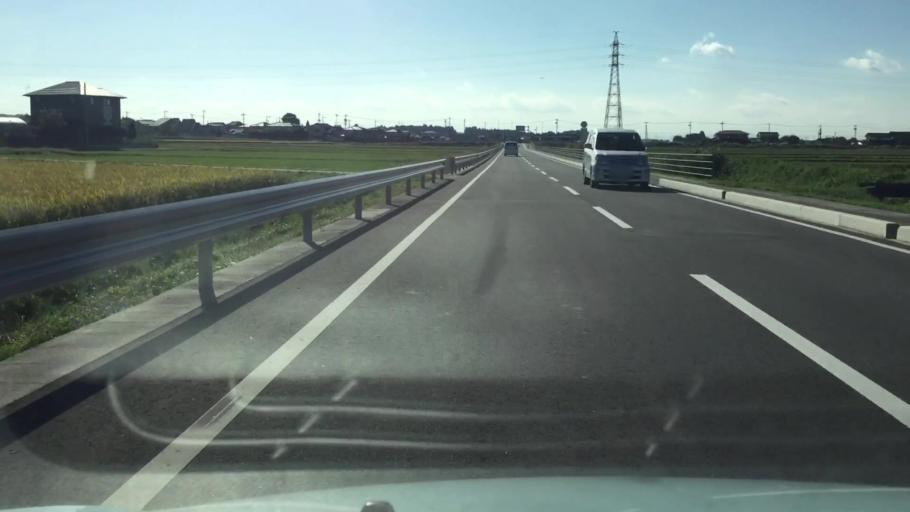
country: JP
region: Tochigi
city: Ujiie
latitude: 36.6592
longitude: 140.0202
